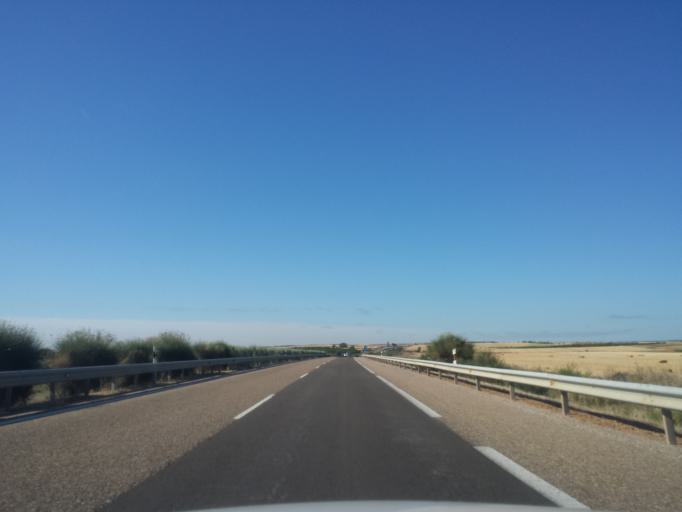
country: ES
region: Castille and Leon
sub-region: Provincia de Zamora
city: Matilla de Arzon
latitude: 42.1409
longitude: -5.6406
